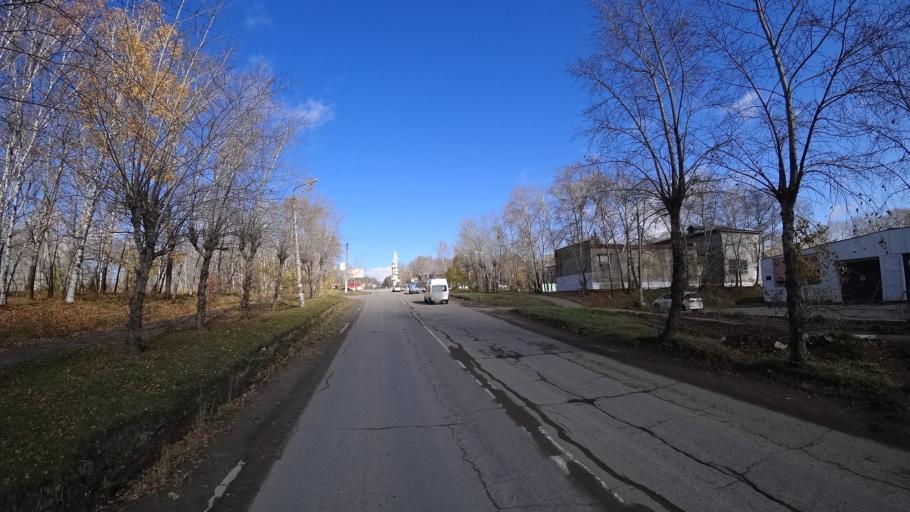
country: RU
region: Khabarovsk Krai
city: Amursk
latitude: 50.2286
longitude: 136.9014
